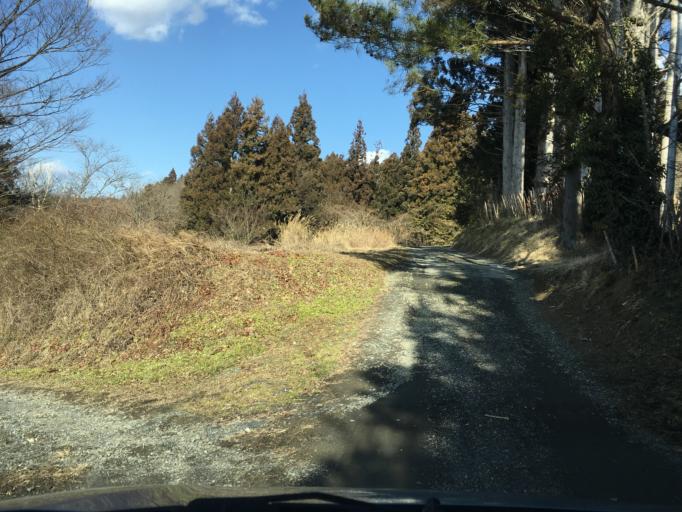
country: JP
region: Iwate
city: Ichinoseki
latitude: 38.8530
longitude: 141.2902
